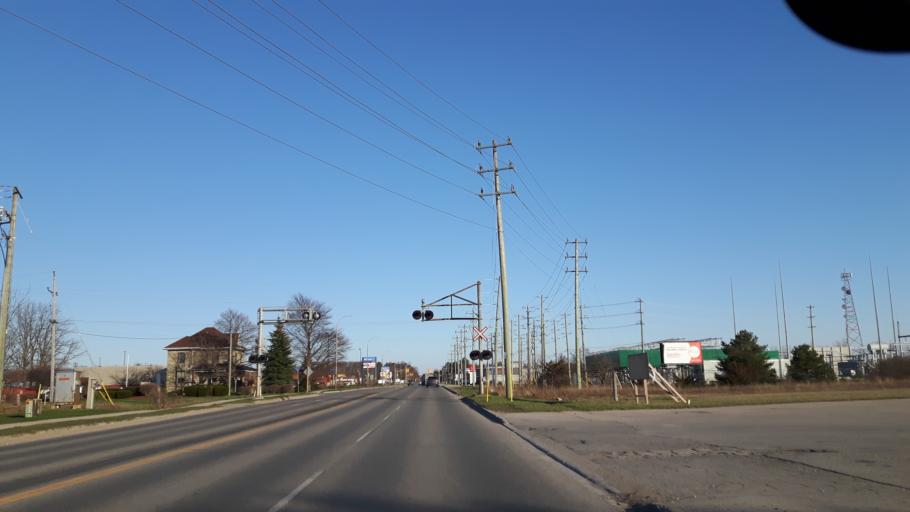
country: CA
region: Ontario
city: Goderich
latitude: 43.7323
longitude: -81.6926
